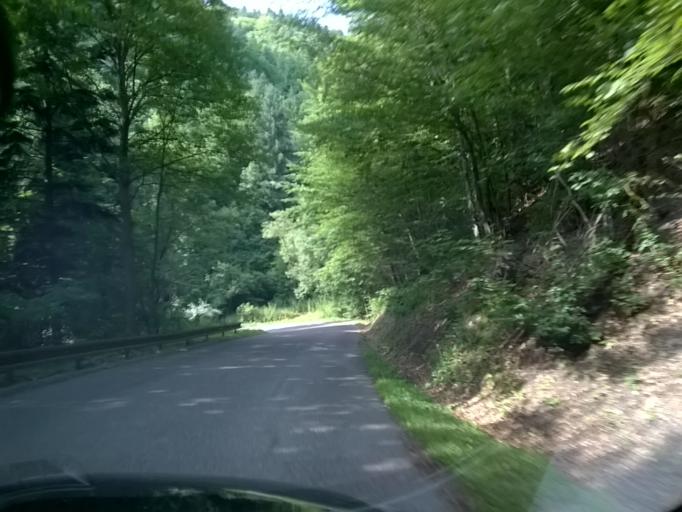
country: SK
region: Banskobystricky
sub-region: Okres Banska Bystrica
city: Banska Stiavnica
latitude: 48.4700
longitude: 18.8593
